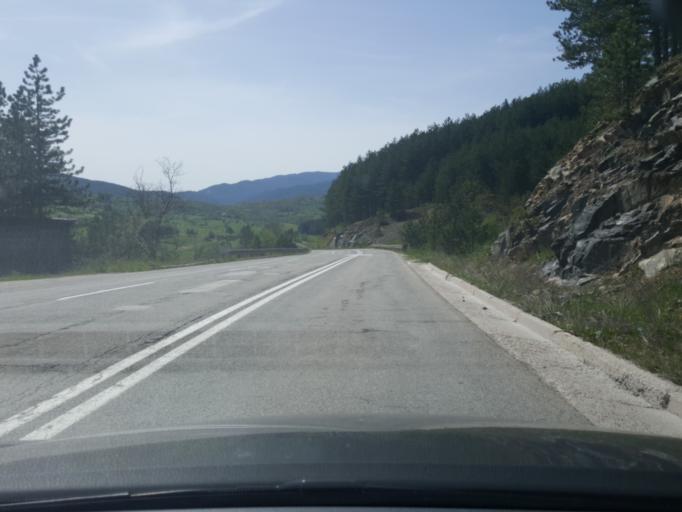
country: RS
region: Central Serbia
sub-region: Zlatiborski Okrug
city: Cajetina
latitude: 43.8343
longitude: 19.6146
